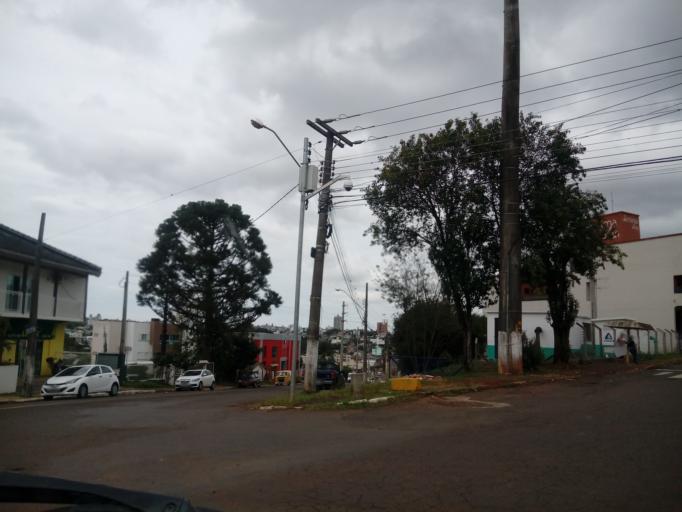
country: BR
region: Santa Catarina
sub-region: Chapeco
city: Chapeco
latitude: -27.0798
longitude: -52.6135
